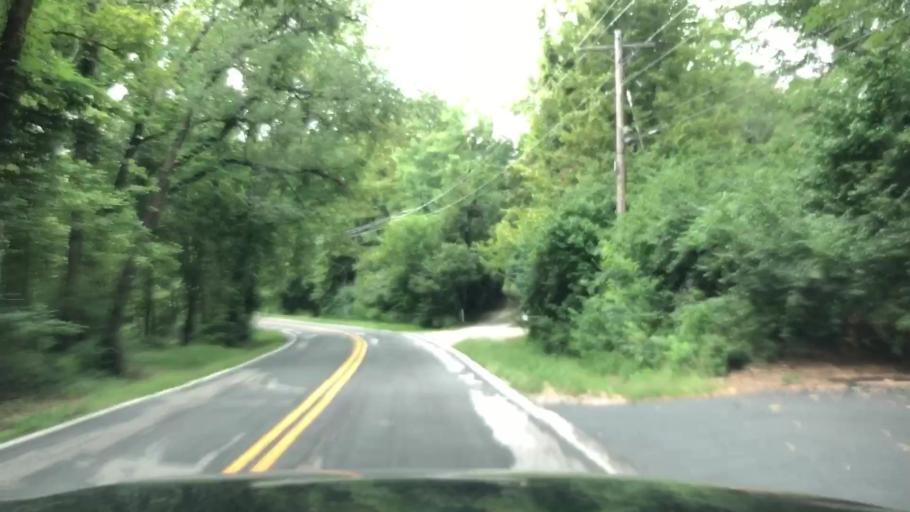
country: US
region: Missouri
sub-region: Saint Louis County
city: Hazelwood
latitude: 38.8152
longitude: -90.3747
